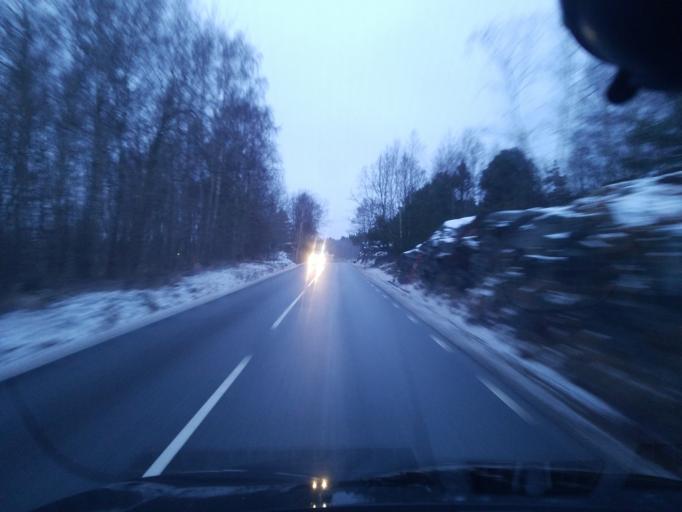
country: SE
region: Vaestra Goetaland
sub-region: Lysekils Kommun
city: Lysekil
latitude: 58.2942
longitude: 11.4769
